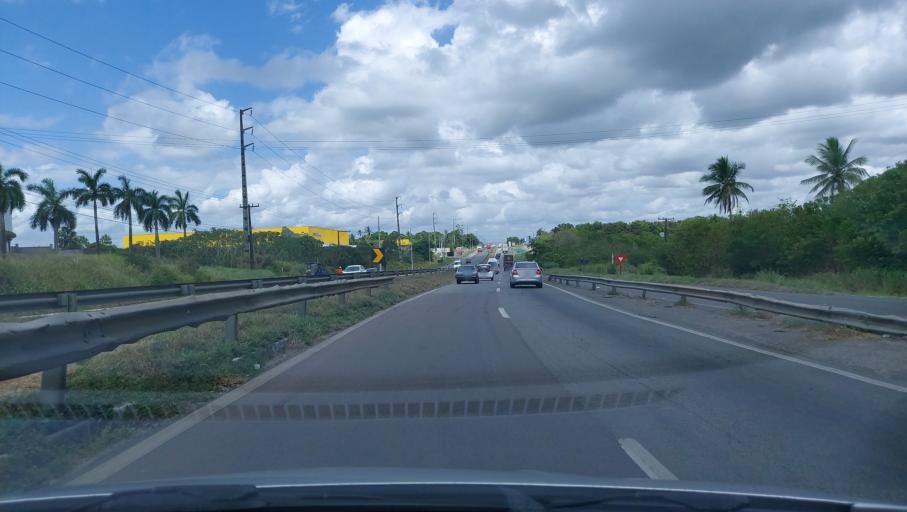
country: BR
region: Bahia
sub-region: Conceicao Do Jacuipe
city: Conceicao do Jacuipe
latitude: -12.3370
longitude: -38.8499
